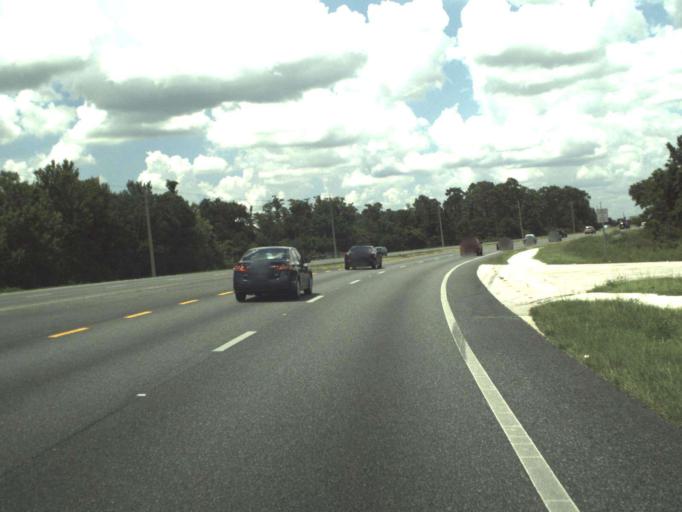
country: US
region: Florida
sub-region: Orange County
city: Fairview Shores
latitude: 28.5615
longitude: -81.4154
